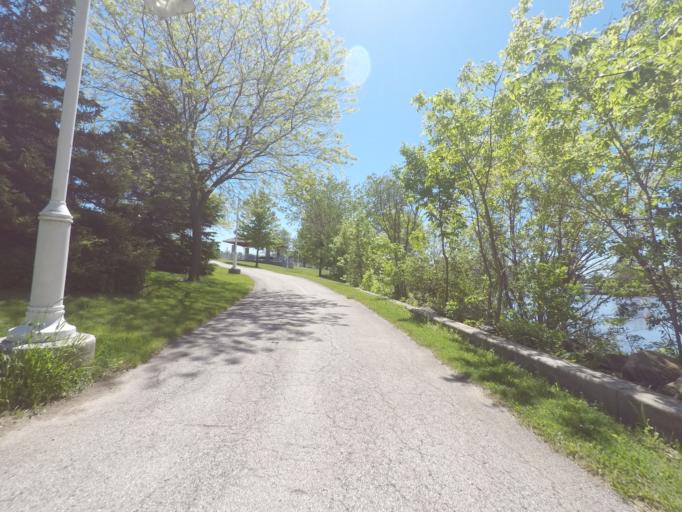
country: US
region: Wisconsin
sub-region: Sheboygan County
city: Sheboygan
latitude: 43.7553
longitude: -87.7214
